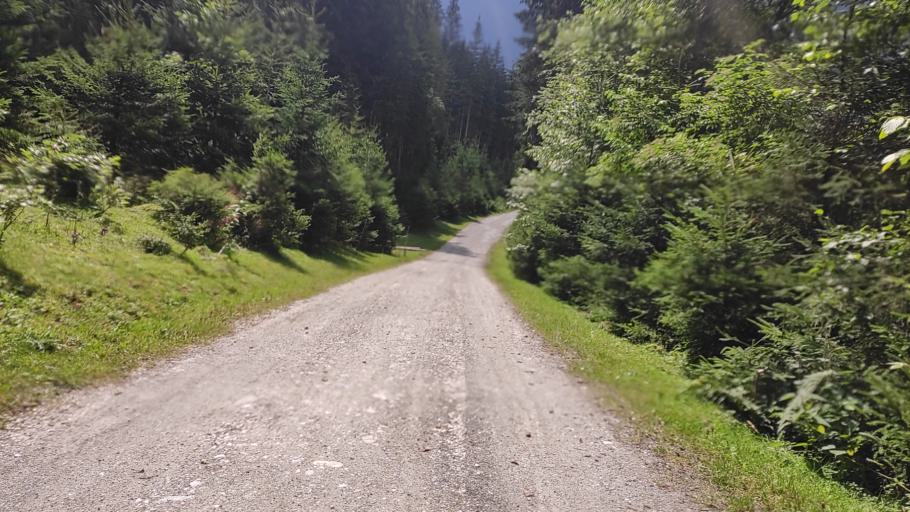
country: AT
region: Salzburg
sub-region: Politischer Bezirk Zell am See
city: Krimml
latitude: 47.2180
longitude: 12.1788
